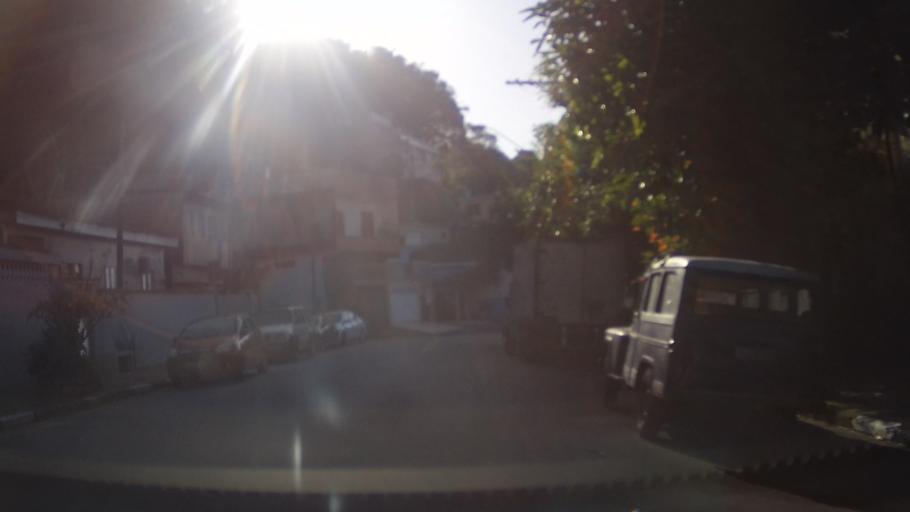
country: BR
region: Sao Paulo
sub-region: Santos
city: Santos
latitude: -23.9397
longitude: -46.3399
